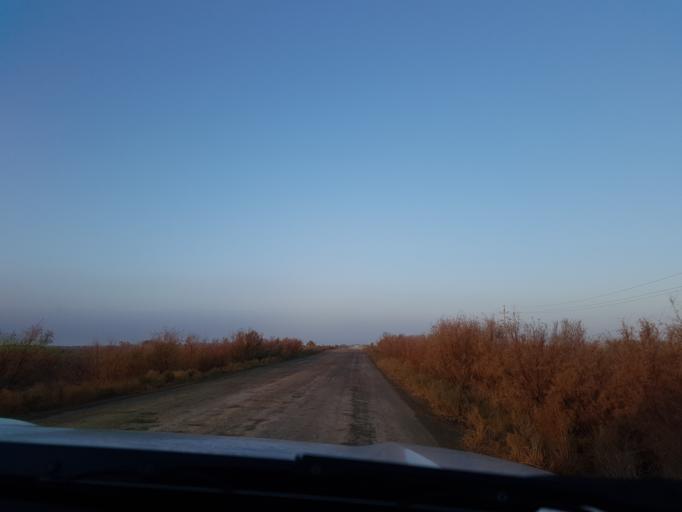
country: TM
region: Dasoguz
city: Koeneuergench
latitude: 41.8449
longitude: 58.6001
